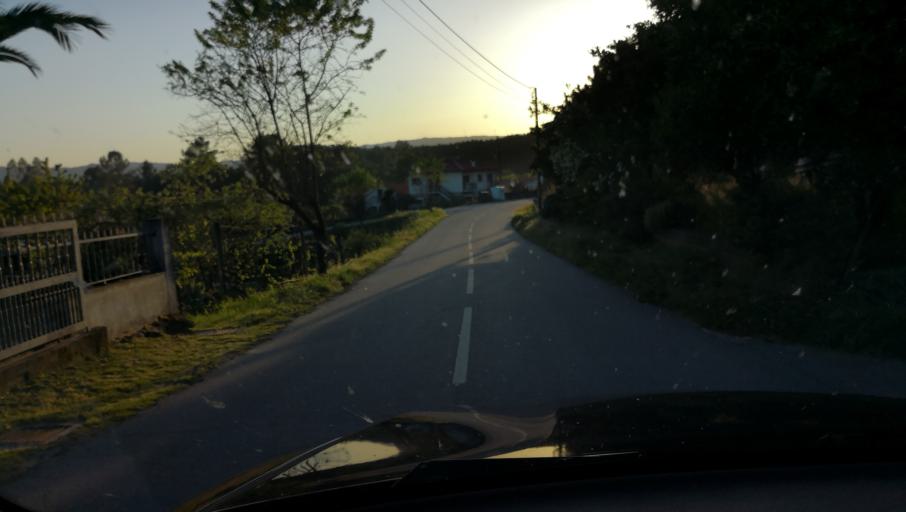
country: PT
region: Vila Real
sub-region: Mondim de Basto
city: Mondim de Basto
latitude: 41.4073
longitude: -7.9248
